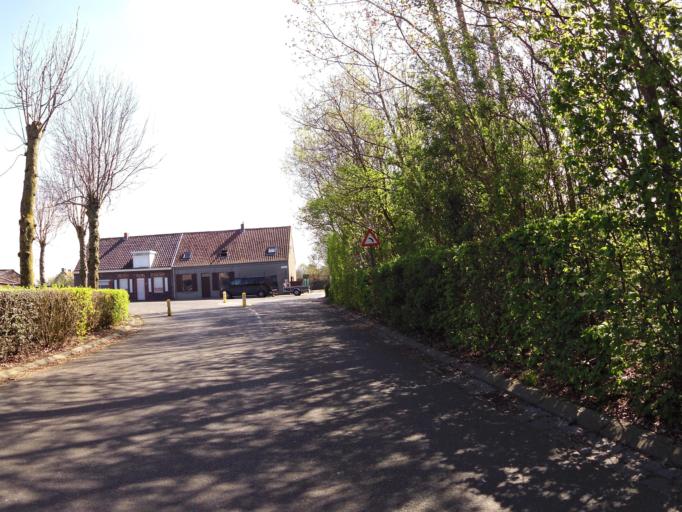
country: BE
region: Flanders
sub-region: Provincie West-Vlaanderen
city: Ichtegem
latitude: 51.1246
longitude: 3.0245
